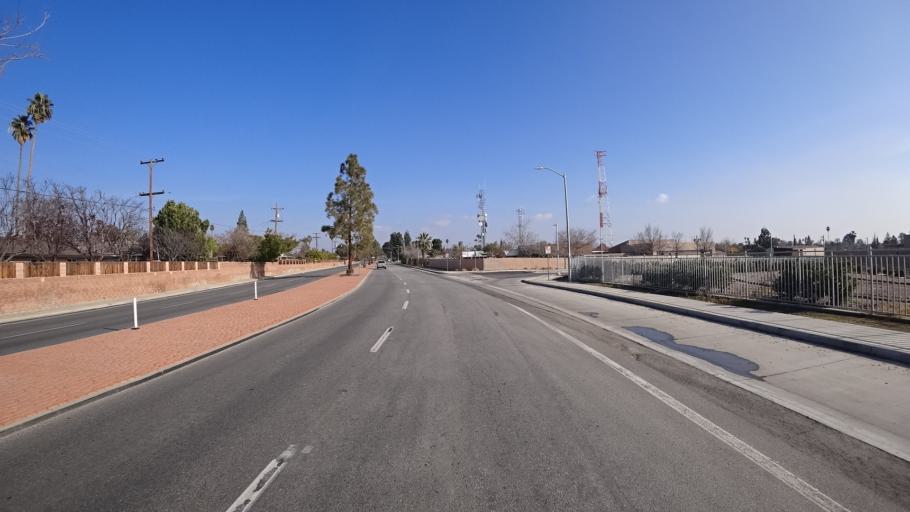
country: US
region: California
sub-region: Kern County
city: Oildale
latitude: 35.4124
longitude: -118.9659
